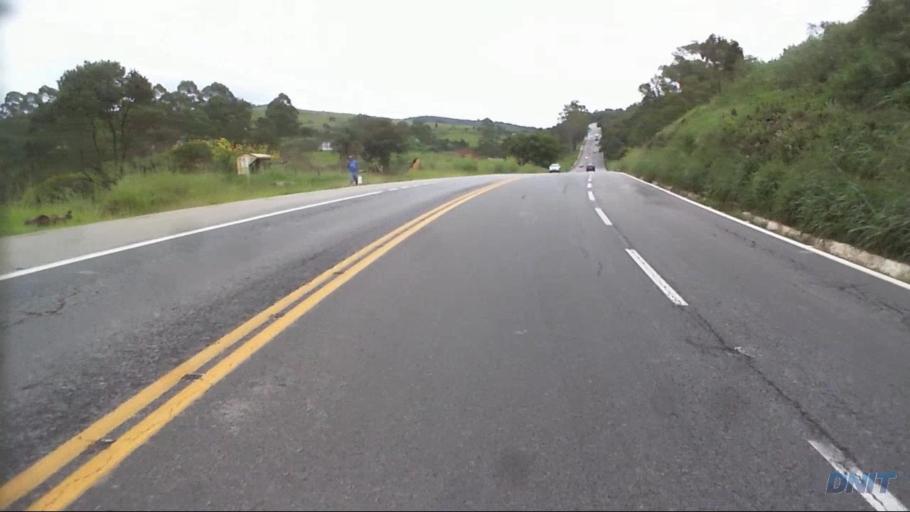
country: BR
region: Minas Gerais
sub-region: Joao Monlevade
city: Joao Monlevade
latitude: -19.8513
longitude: -43.2926
